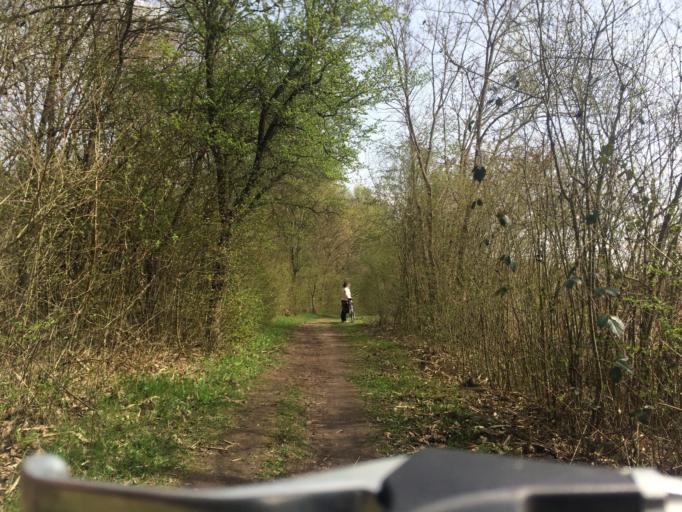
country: DE
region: Hesse
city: Morfelden-Walldorf
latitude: 49.9880
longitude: 8.5961
